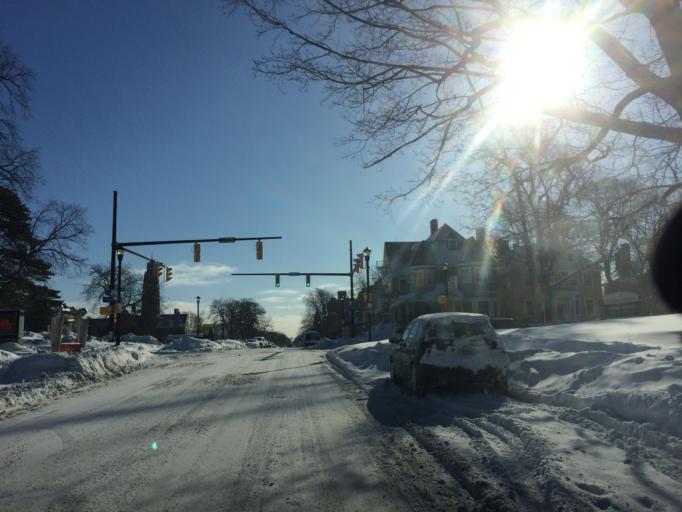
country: US
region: New York
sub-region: Monroe County
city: Rochester
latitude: 43.1578
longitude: -77.5913
